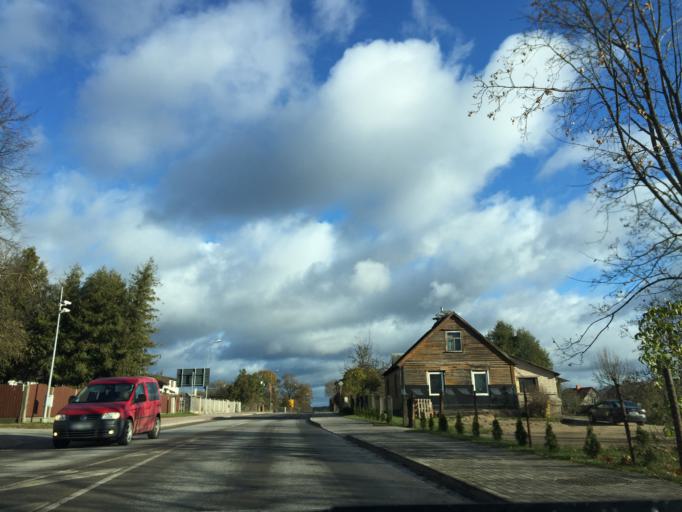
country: LV
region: Tukuma Rajons
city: Tukums
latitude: 56.9676
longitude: 23.1739
